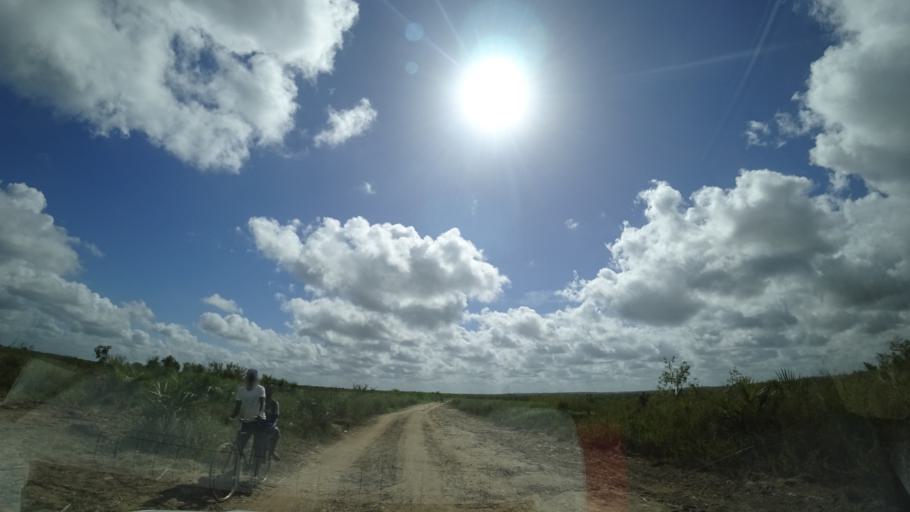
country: MZ
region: Sofala
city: Dondo
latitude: -19.4013
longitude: 34.5678
